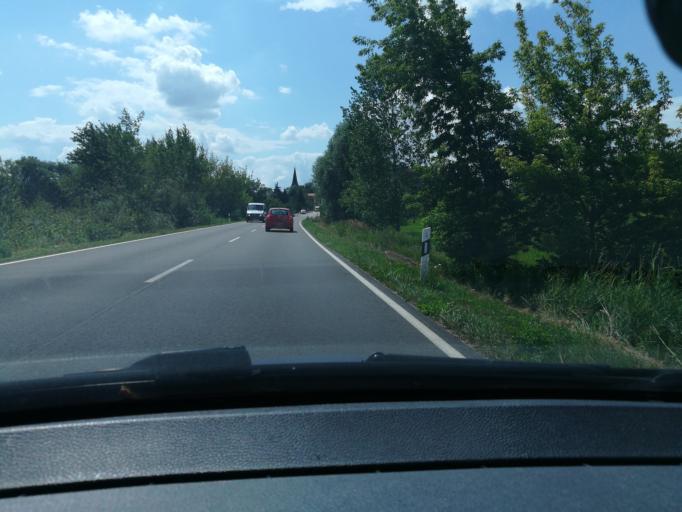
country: DE
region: Saxony-Anhalt
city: Zielitz
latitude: 52.2908
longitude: 11.6835
